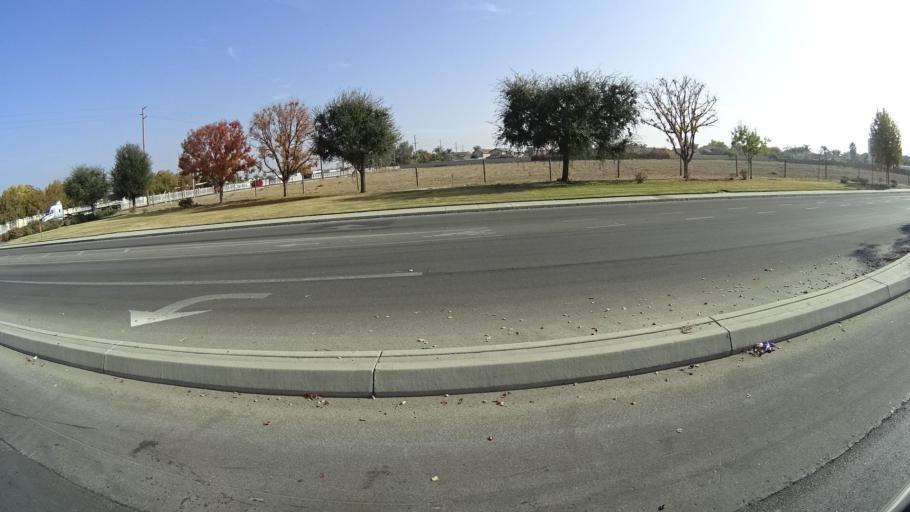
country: US
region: California
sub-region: Kern County
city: Delano
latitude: 35.7897
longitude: -119.2229
